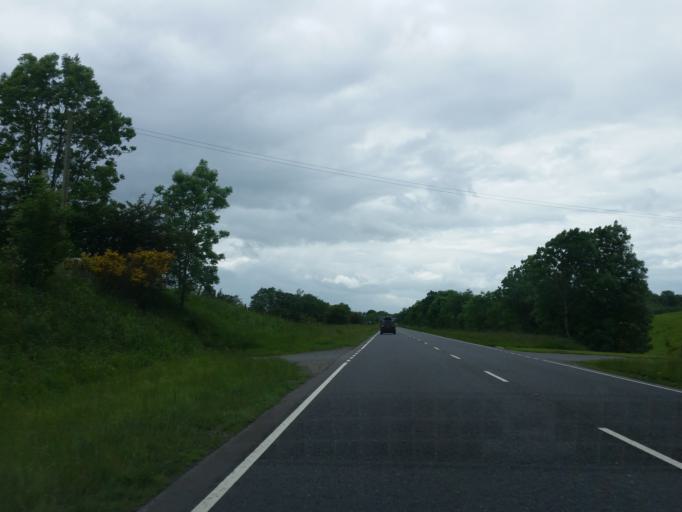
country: GB
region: Northern Ireland
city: Fivemiletown
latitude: 54.3852
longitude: -7.2558
